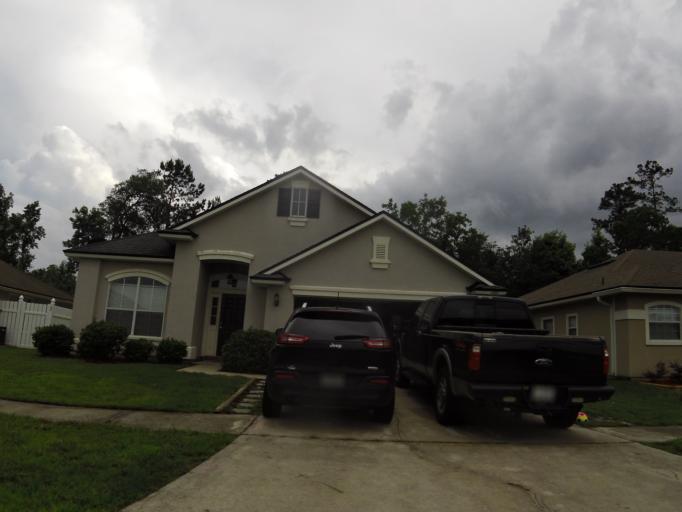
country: US
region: Florida
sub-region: Nassau County
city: Callahan
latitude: 30.5697
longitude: -81.8308
